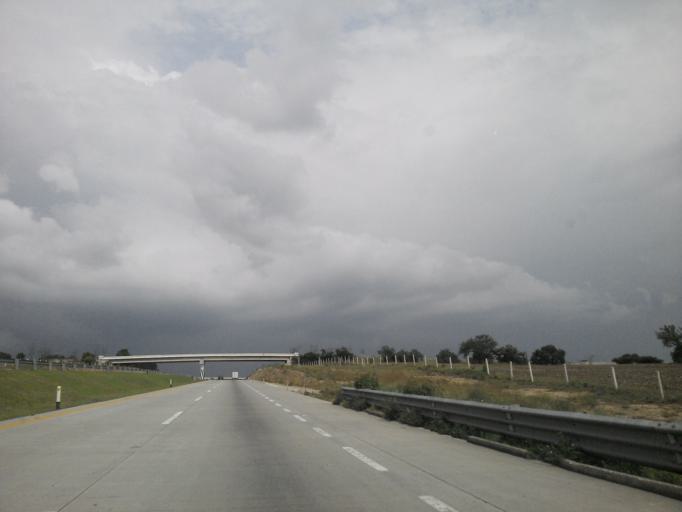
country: MX
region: Mexico
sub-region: Hueypoxtla
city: Santa Maria Ajoloapan
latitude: 19.9682
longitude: -99.0973
